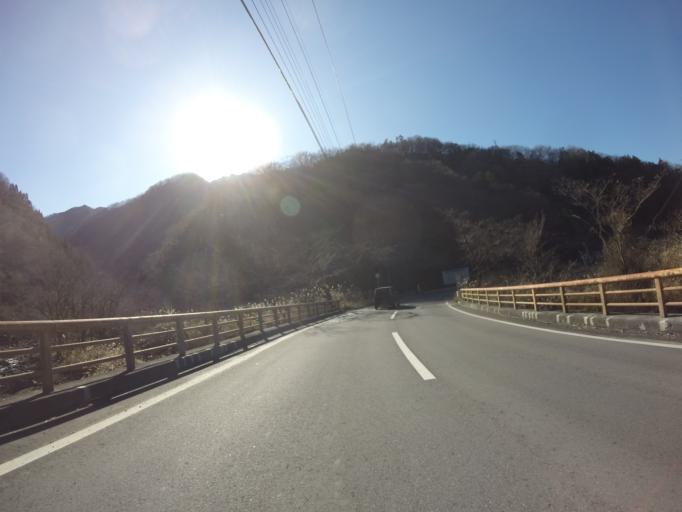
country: JP
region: Yamanashi
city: Ryuo
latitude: 35.4224
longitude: 138.4054
